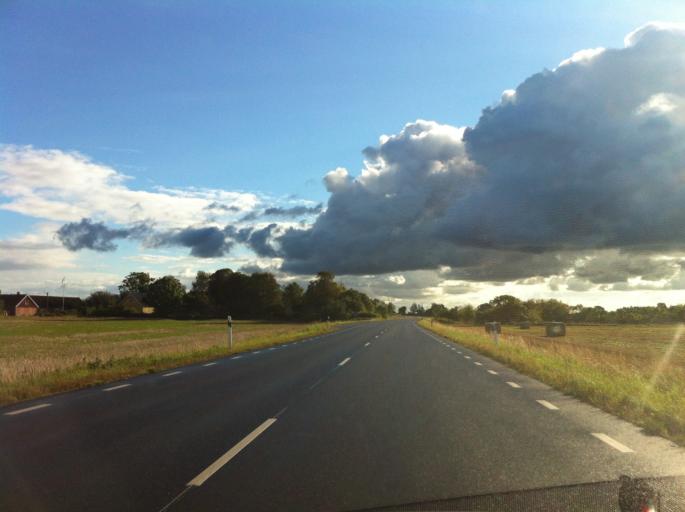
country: SE
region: Skane
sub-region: Svalovs Kommun
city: Svaloev
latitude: 55.9311
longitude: 13.2126
